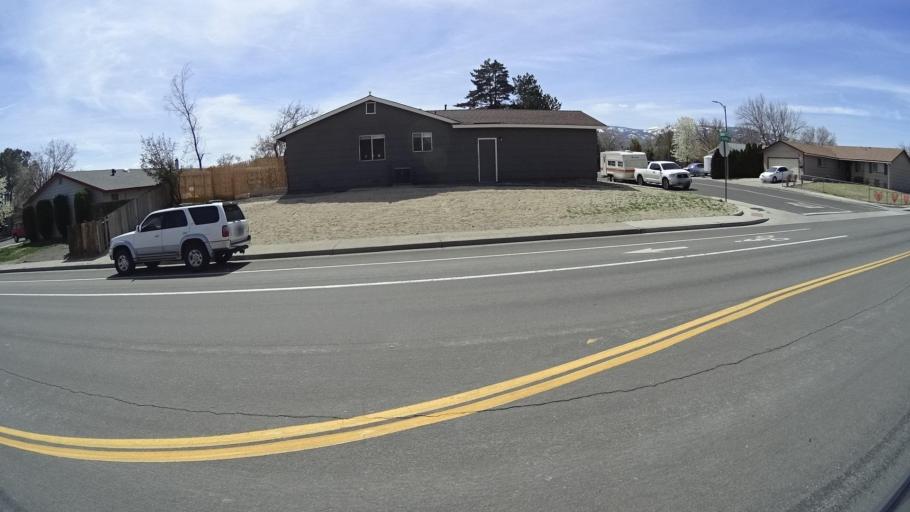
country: US
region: Nevada
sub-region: Washoe County
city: Reno
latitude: 39.5307
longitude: -119.8542
